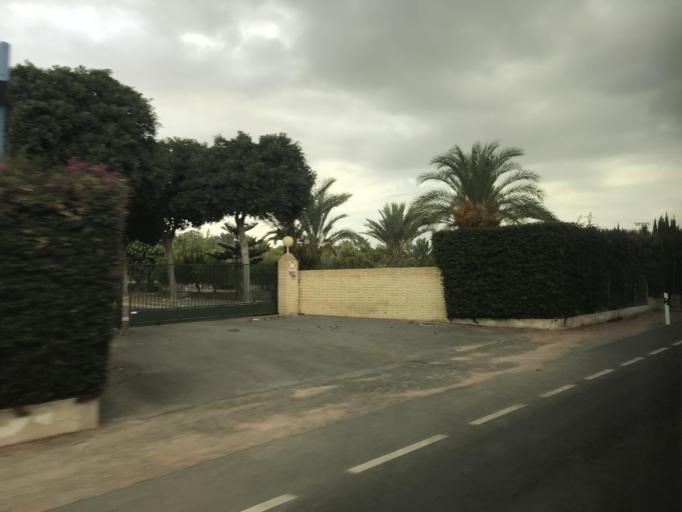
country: ES
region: Valencia
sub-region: Provincia de Alicante
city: Guardamar del Segura
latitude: 38.1262
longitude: -0.6513
